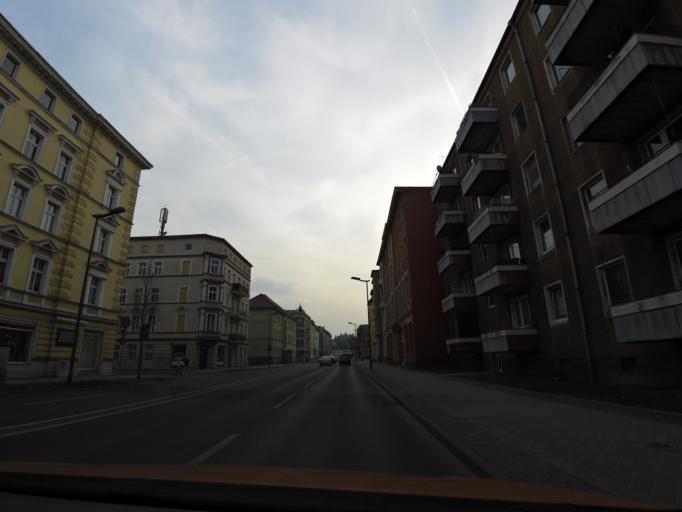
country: DE
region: Brandenburg
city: Frankfurt (Oder)
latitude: 52.3368
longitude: 14.5381
